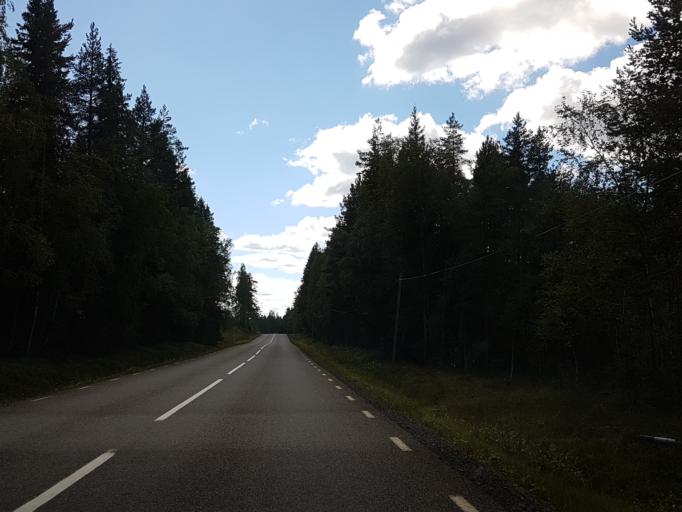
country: SE
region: Vaesterbotten
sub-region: Umea Kommun
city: Saevar
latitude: 64.1317
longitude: 20.5537
